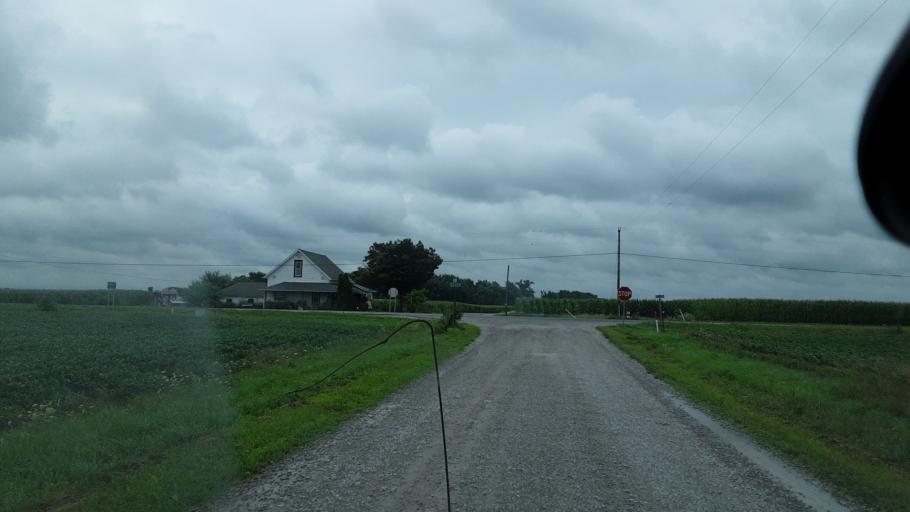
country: US
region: Indiana
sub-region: Wells County
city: Ossian
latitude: 40.8315
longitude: -85.0723
